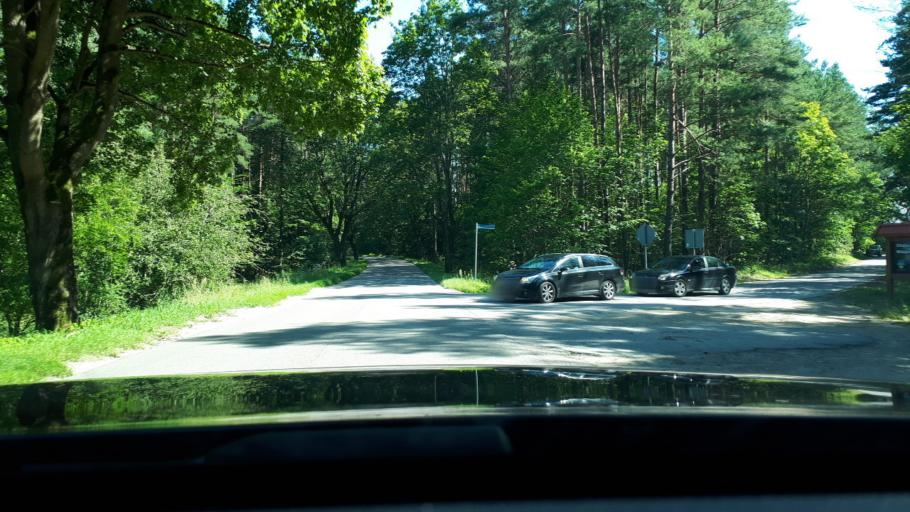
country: PL
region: Warmian-Masurian Voivodeship
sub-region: Powiat olsztynski
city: Stawiguda
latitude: 53.6117
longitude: 20.4183
